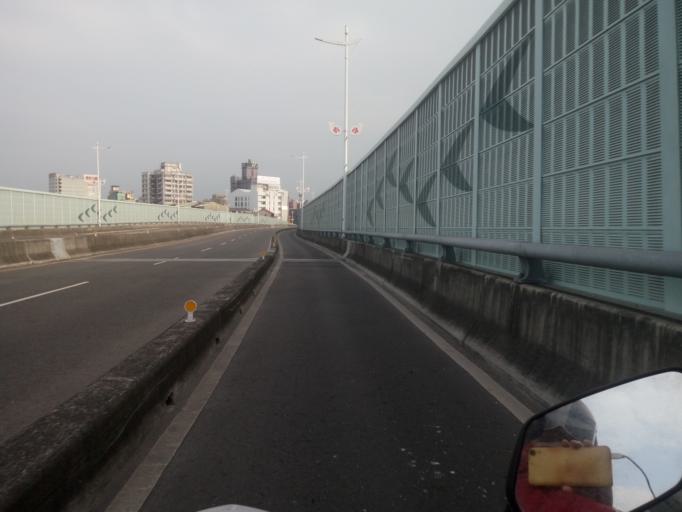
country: TW
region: Taiwan
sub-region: Chiayi
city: Jiayi Shi
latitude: 23.4746
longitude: 120.4346
